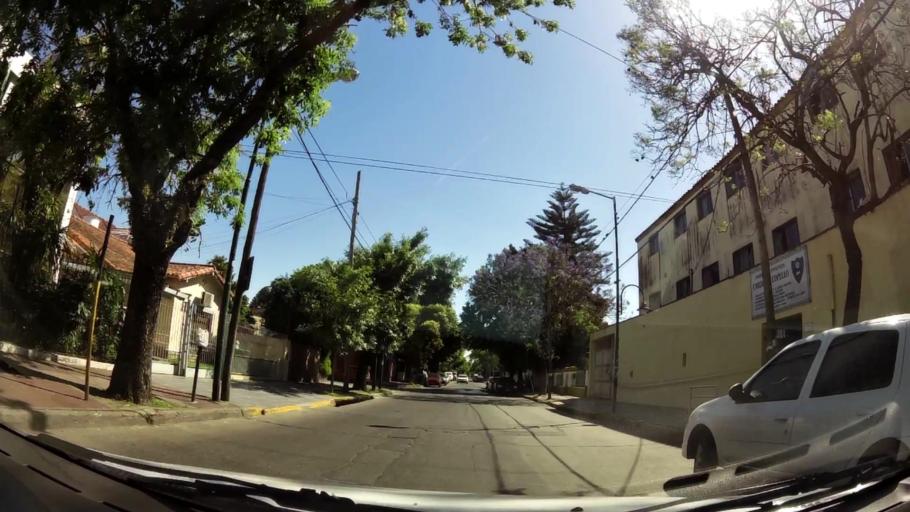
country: AR
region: Buenos Aires
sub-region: Partido de San Isidro
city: San Isidro
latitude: -34.4529
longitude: -58.5287
